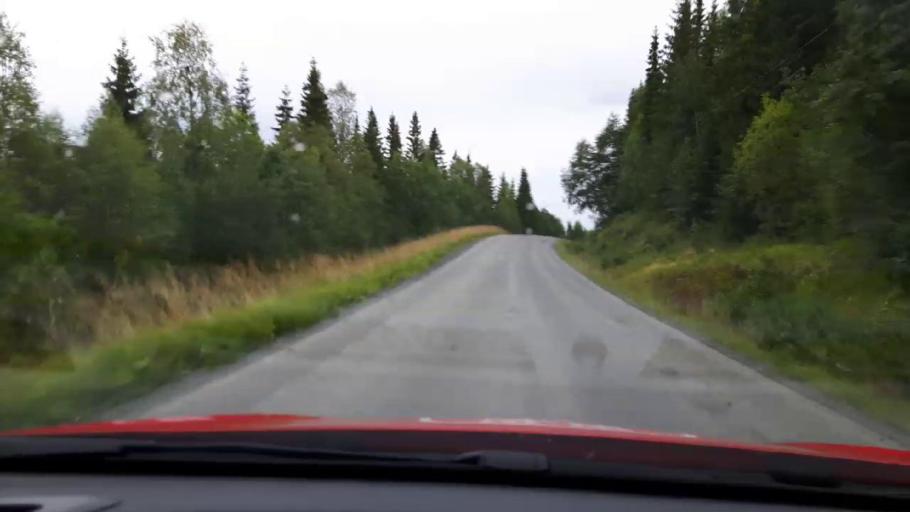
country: SE
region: Jaemtland
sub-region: Are Kommun
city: Jarpen
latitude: 63.4156
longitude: 13.3543
